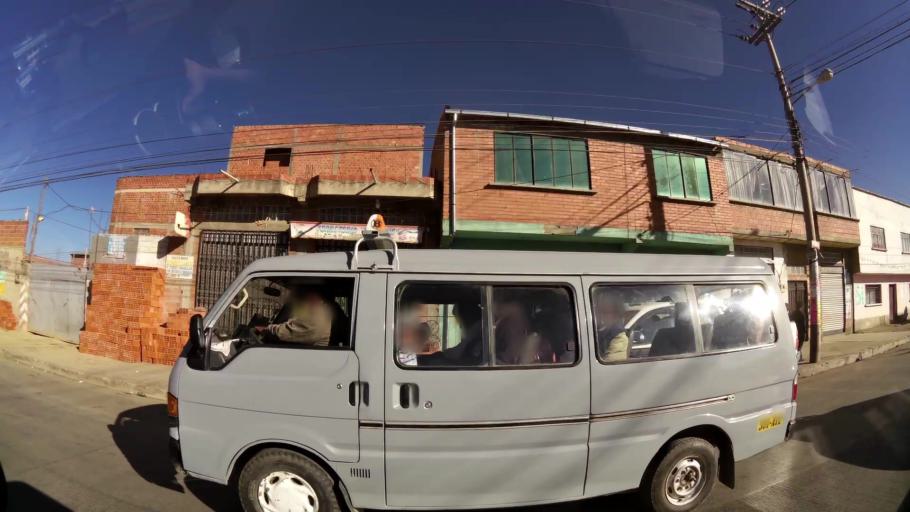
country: BO
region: La Paz
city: La Paz
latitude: -16.5233
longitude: -68.1585
